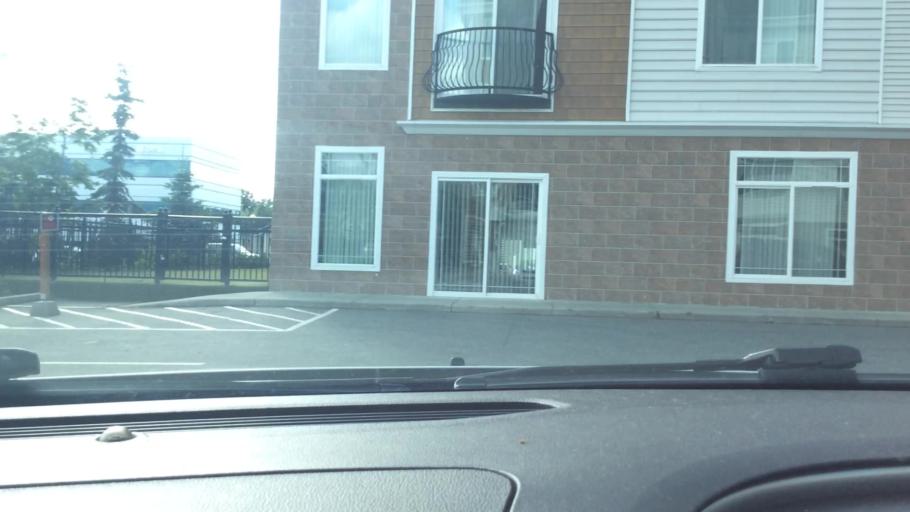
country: US
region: Alaska
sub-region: Anchorage Municipality
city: Anchorage
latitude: 61.2063
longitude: -149.8822
